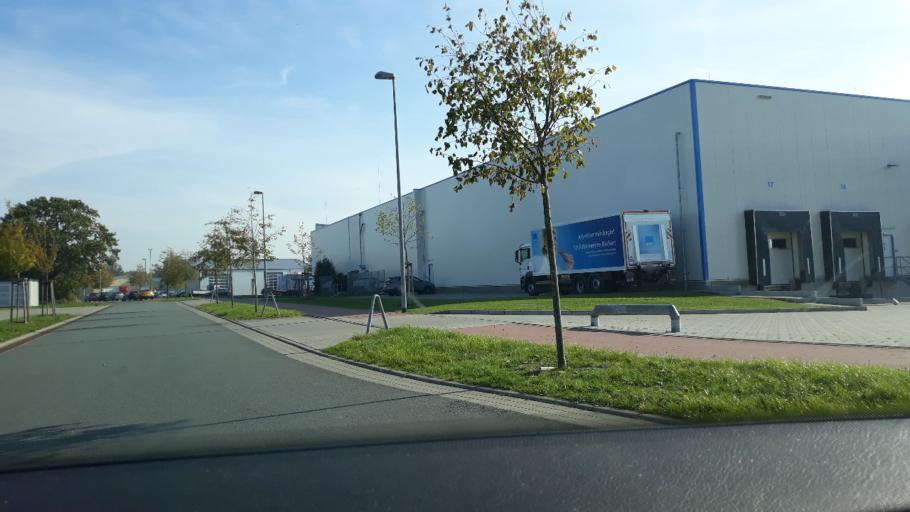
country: DE
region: Schleswig-Holstein
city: Kropp
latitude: 54.4187
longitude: 9.5224
